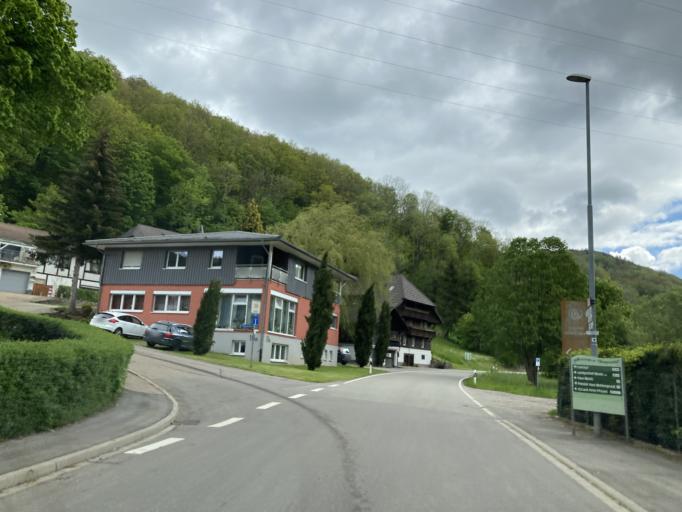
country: DE
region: Baden-Wuerttemberg
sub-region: Freiburg Region
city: Muhlenbach
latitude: 48.2125
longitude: 8.1459
